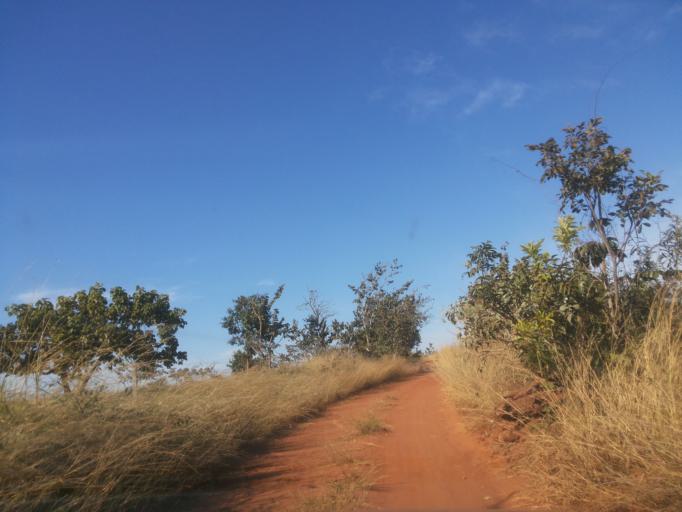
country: BR
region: Minas Gerais
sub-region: Ituiutaba
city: Ituiutaba
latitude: -19.1214
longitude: -49.3958
